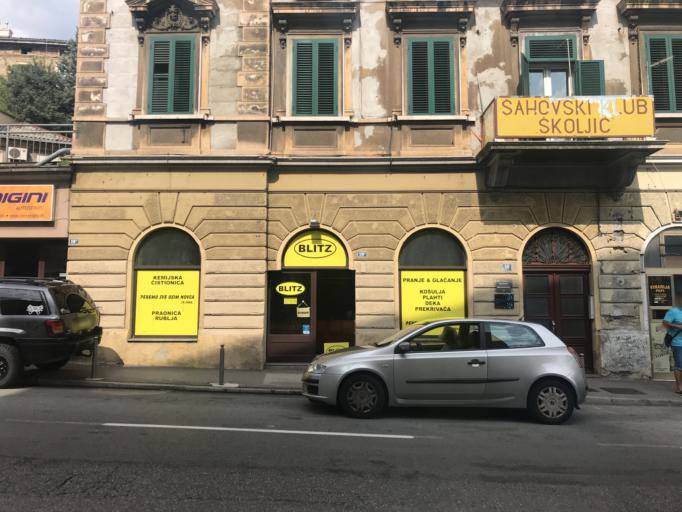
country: HR
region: Primorsko-Goranska
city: Drenova
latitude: 45.3287
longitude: 14.4461
